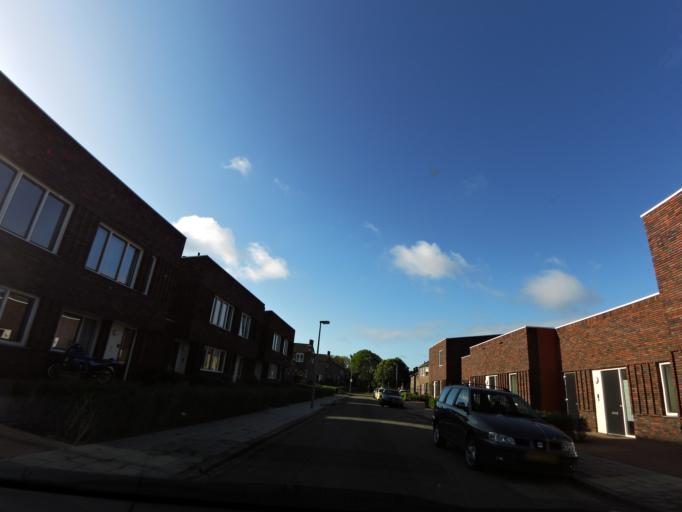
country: NL
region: Limburg
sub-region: Gemeente Voerendaal
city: Ubachsberg
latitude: 50.8524
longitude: 5.9458
